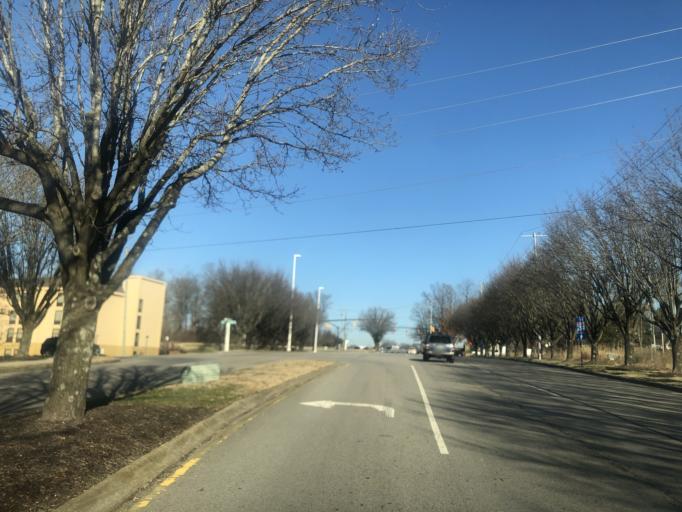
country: US
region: Tennessee
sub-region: Rutherford County
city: La Vergne
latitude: 36.0440
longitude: -86.6469
